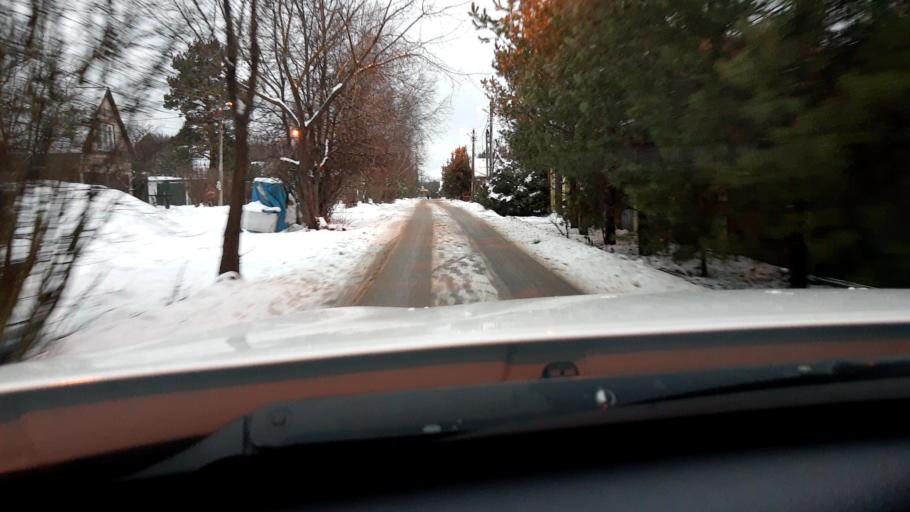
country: RU
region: Moskovskaya
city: Krasnogorsk
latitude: 55.8649
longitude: 37.3145
